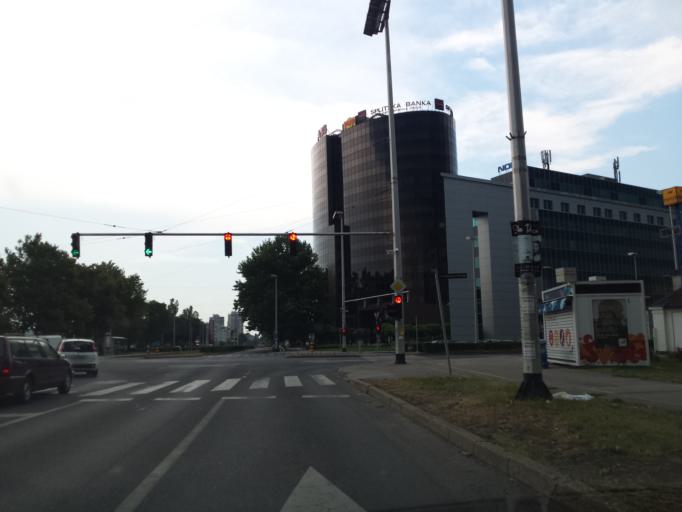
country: HR
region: Grad Zagreb
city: Novi Zagreb
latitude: 45.8022
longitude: 16.0105
